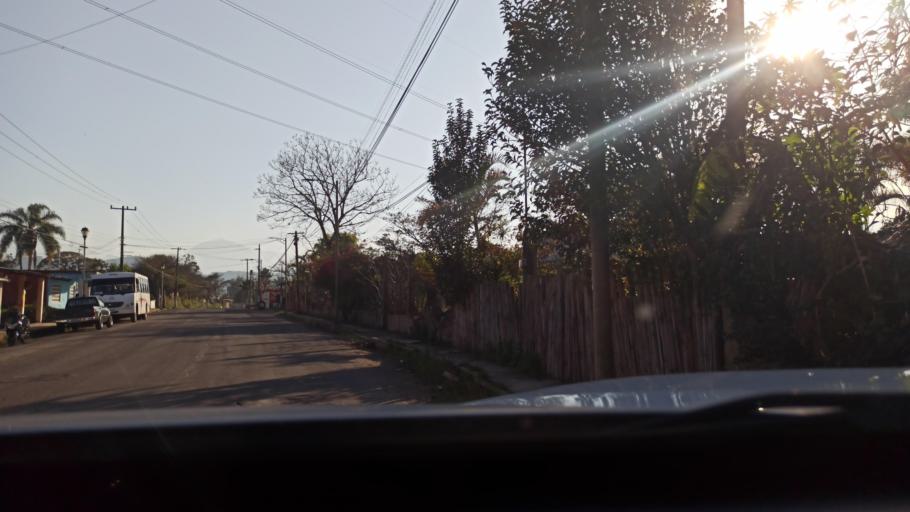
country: MX
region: Veracruz
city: Atzacan
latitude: 18.8986
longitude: -97.0871
